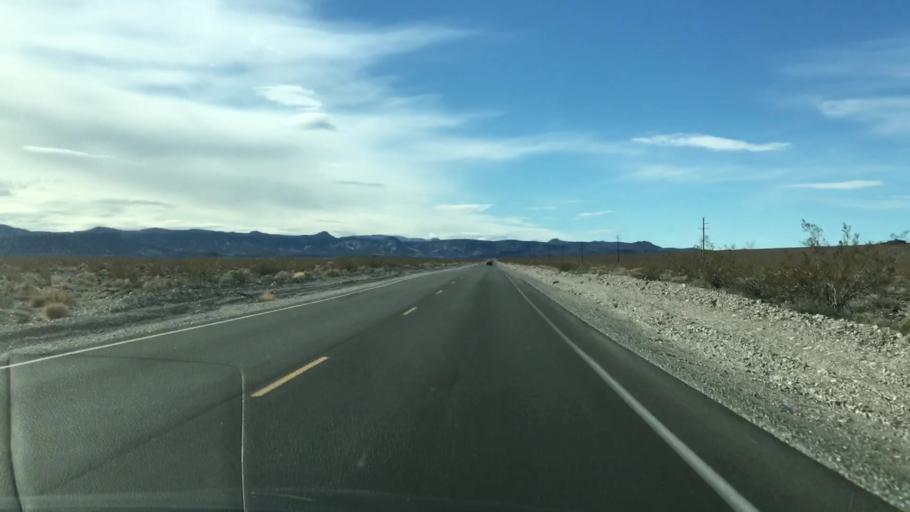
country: US
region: Nevada
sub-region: Nye County
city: Pahrump
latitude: 36.3033
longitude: -116.4783
